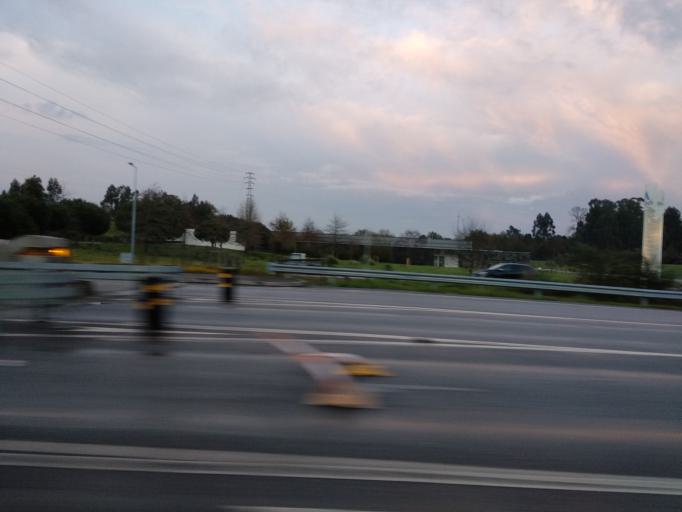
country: PT
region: Braga
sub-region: Vila Nova de Famalicao
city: Calendario
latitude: 41.3879
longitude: -8.5179
